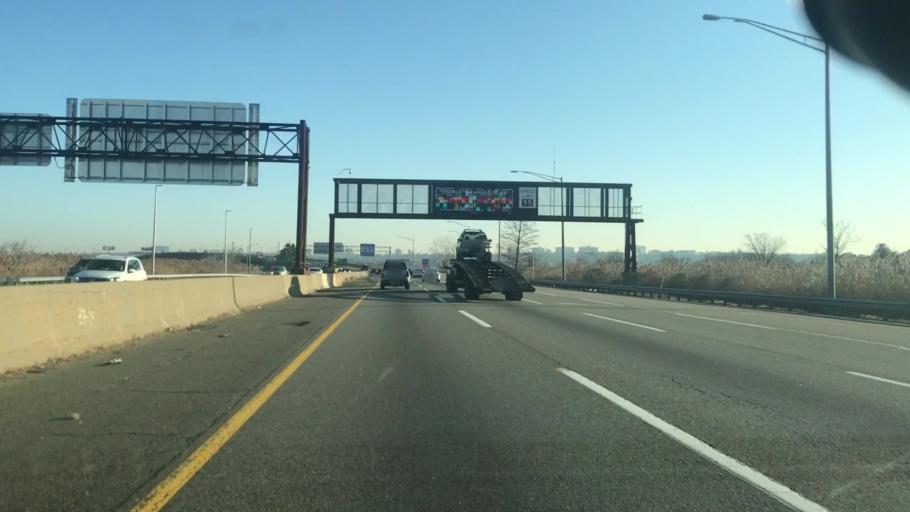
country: US
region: New Jersey
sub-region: Bergen County
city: Moonachie
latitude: 40.8179
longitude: -74.0434
